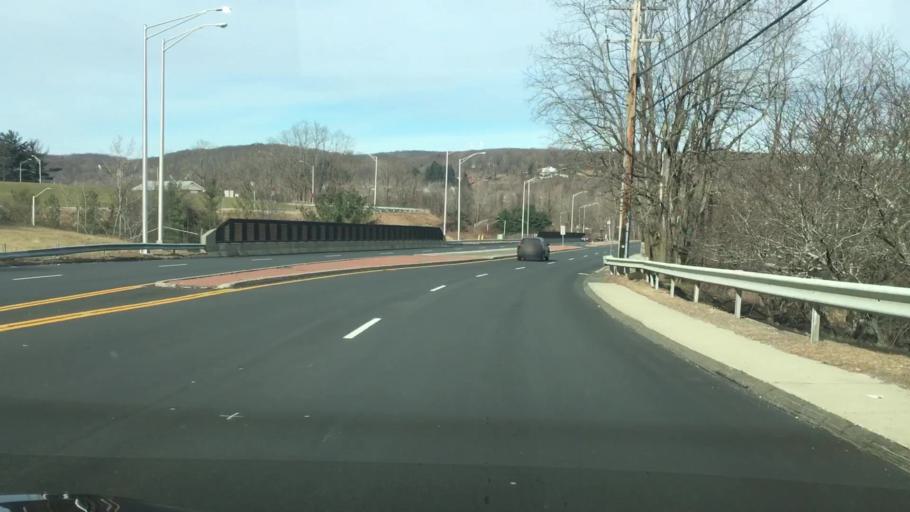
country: US
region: Connecticut
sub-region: Fairfield County
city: Danbury
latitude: 41.3885
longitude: -73.5160
